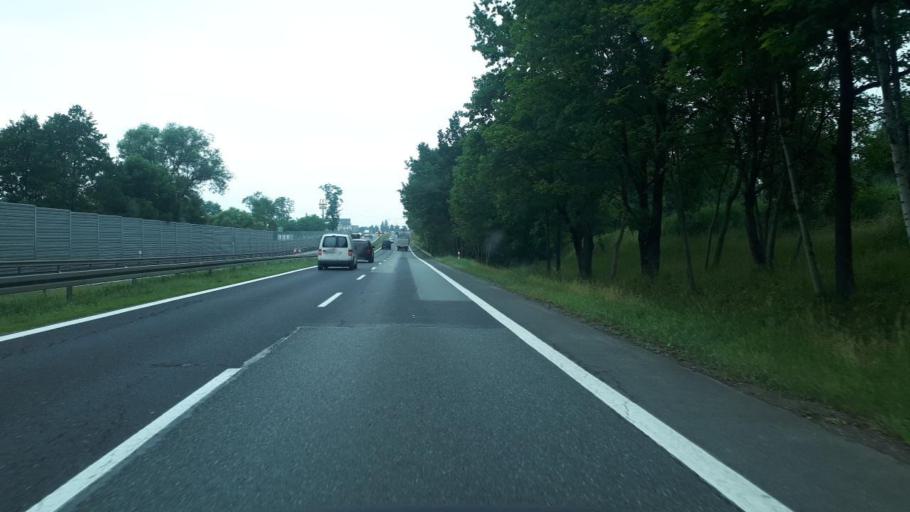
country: PL
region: Silesian Voivodeship
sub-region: Powiat bielski
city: Czechowice-Dziedzice
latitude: 49.8879
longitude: 18.9968
